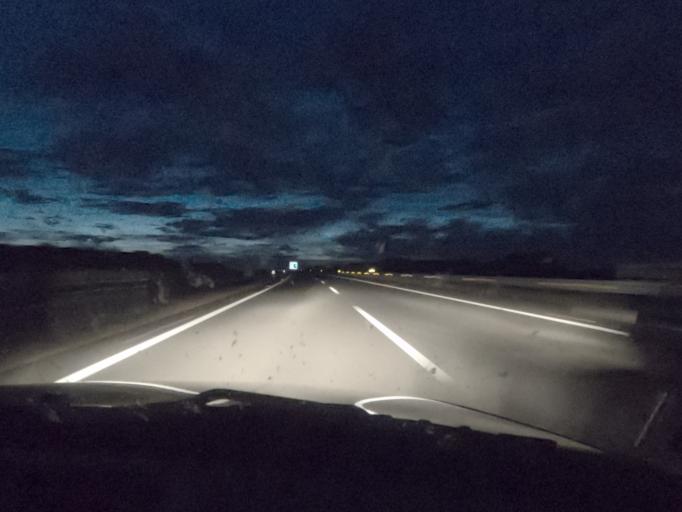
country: ES
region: Extremadura
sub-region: Provincia de Caceres
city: Morcillo
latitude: 39.9871
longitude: -6.4302
